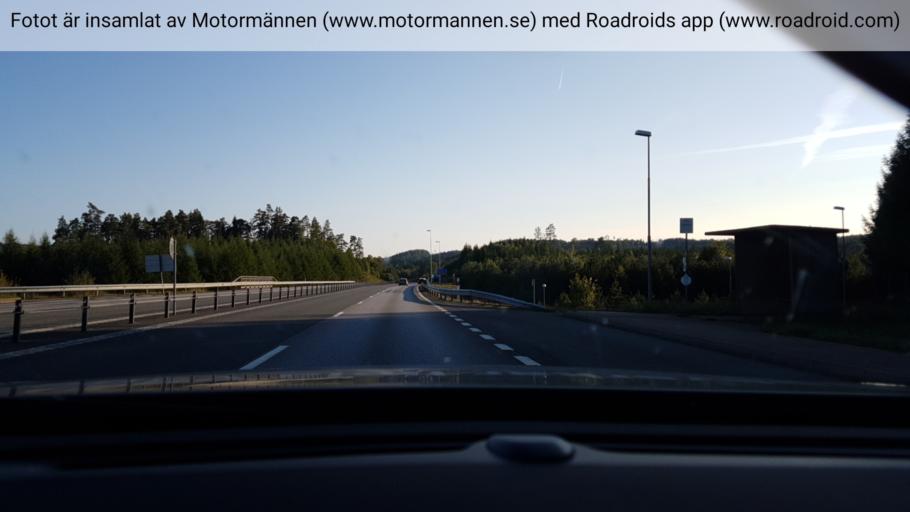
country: SE
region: Halland
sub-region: Hylte Kommun
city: Torup
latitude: 56.8748
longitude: 13.0445
